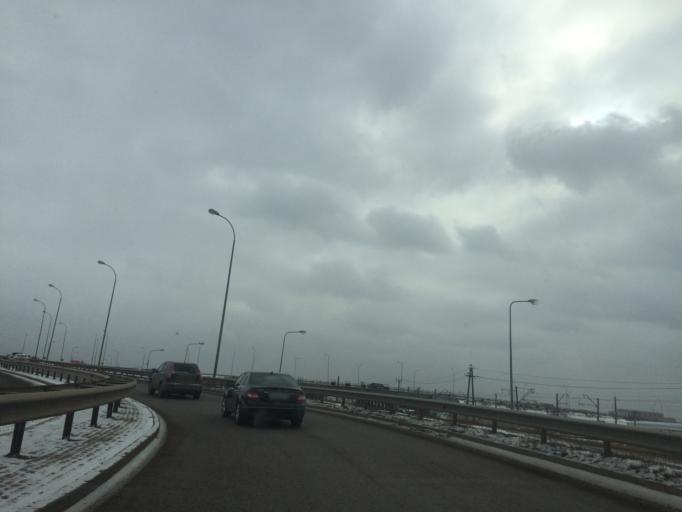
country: KZ
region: Astana Qalasy
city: Astana
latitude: 51.1739
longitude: 71.4797
